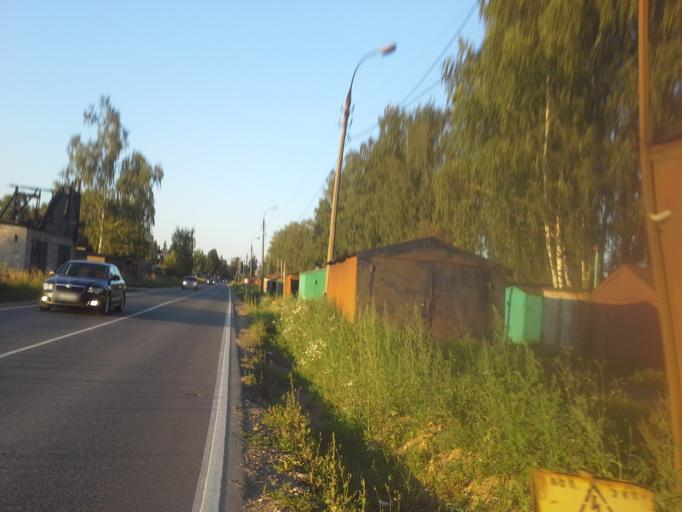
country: RU
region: Moskovskaya
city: Selyatino
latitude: 55.5225
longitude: 36.9651
